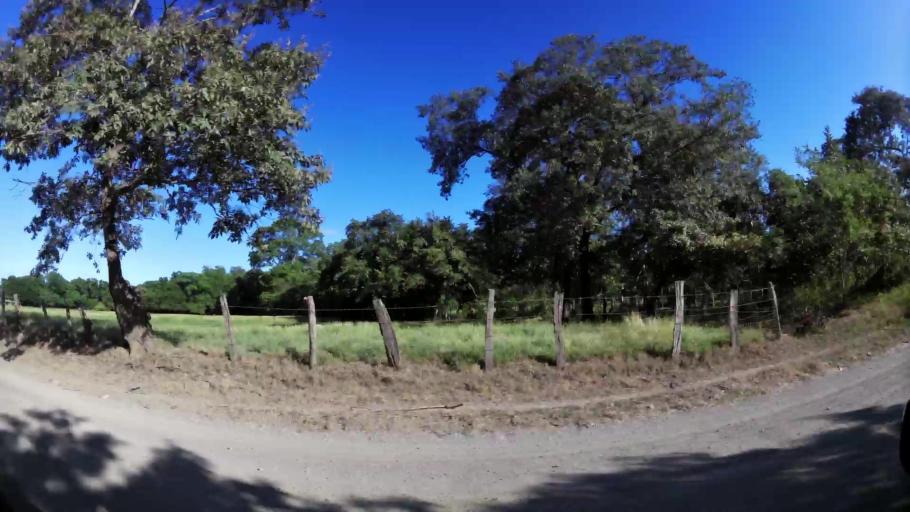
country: CR
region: Guanacaste
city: Sardinal
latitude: 10.4806
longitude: -85.6103
